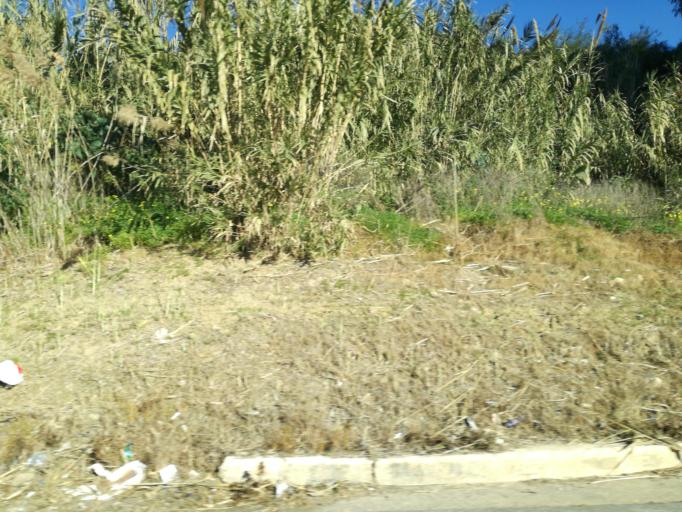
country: IT
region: Sicily
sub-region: Provincia di Caltanissetta
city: Gela
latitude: 37.0680
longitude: 14.2308
